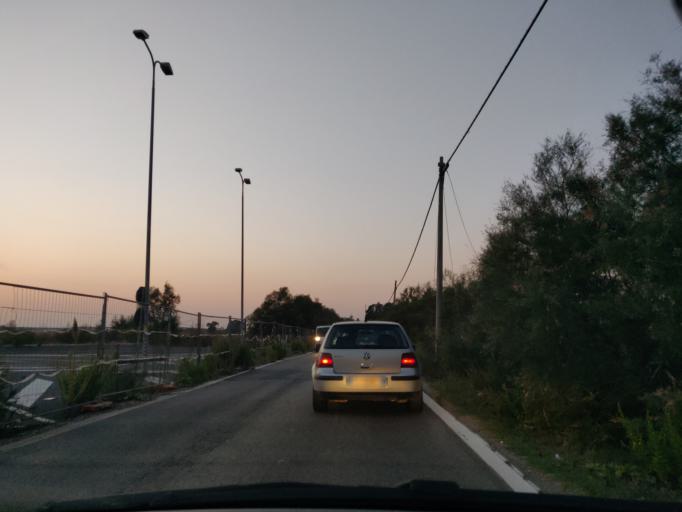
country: IT
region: Latium
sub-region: Citta metropolitana di Roma Capitale
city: Npp 23 (Parco Leonardo)
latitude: 41.8240
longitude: 12.2908
